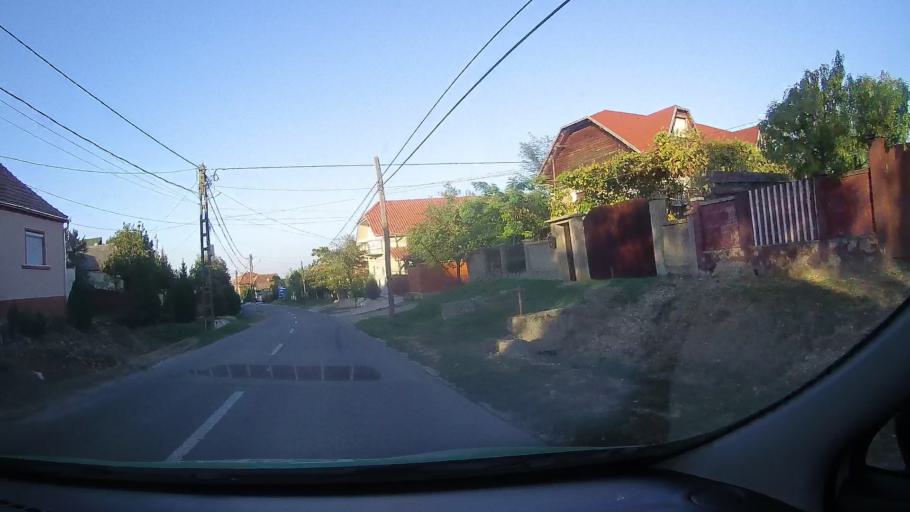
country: RO
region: Bihor
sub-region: Comuna Cetariu
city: Cetariu
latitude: 47.1449
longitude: 21.9998
